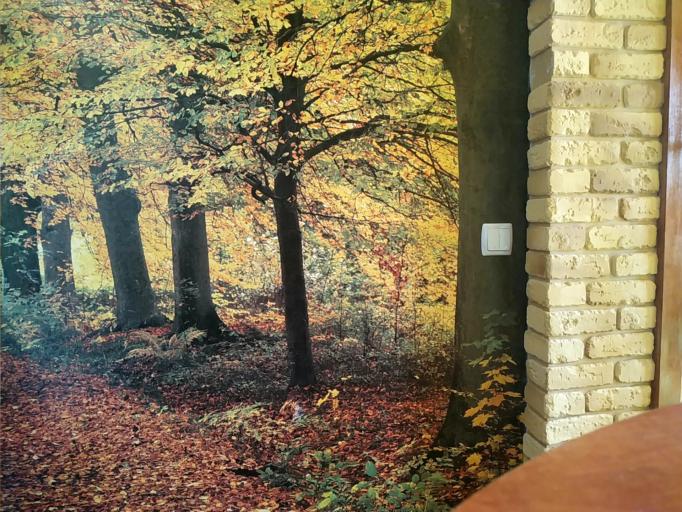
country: RU
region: Jaroslavl
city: Kukoboy
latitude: 58.8789
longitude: 39.7128
